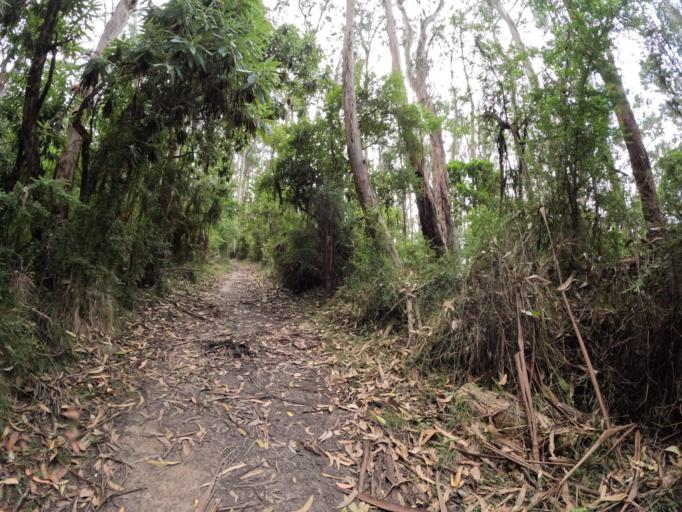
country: AU
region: Victoria
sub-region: Colac-Otway
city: Apollo Bay
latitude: -38.7919
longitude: 143.6159
